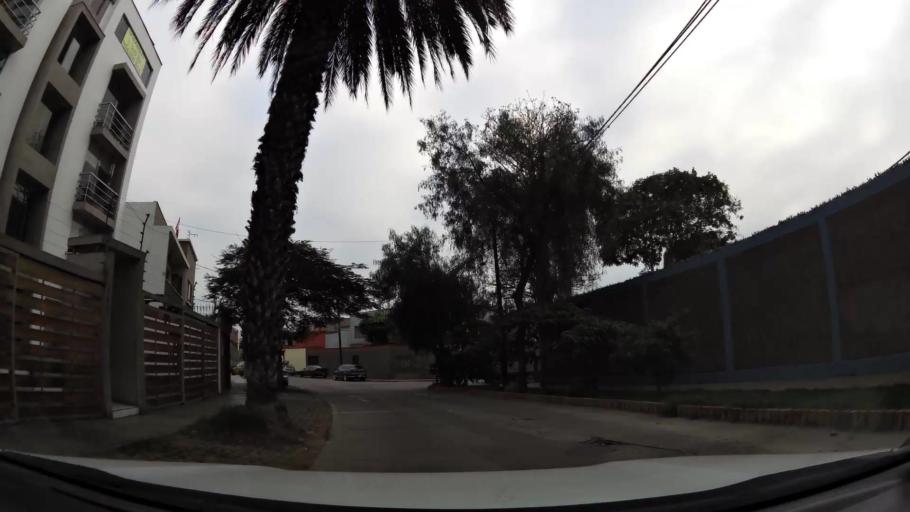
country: PE
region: Lima
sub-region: Lima
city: Surco
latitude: -12.1409
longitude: -77.0194
